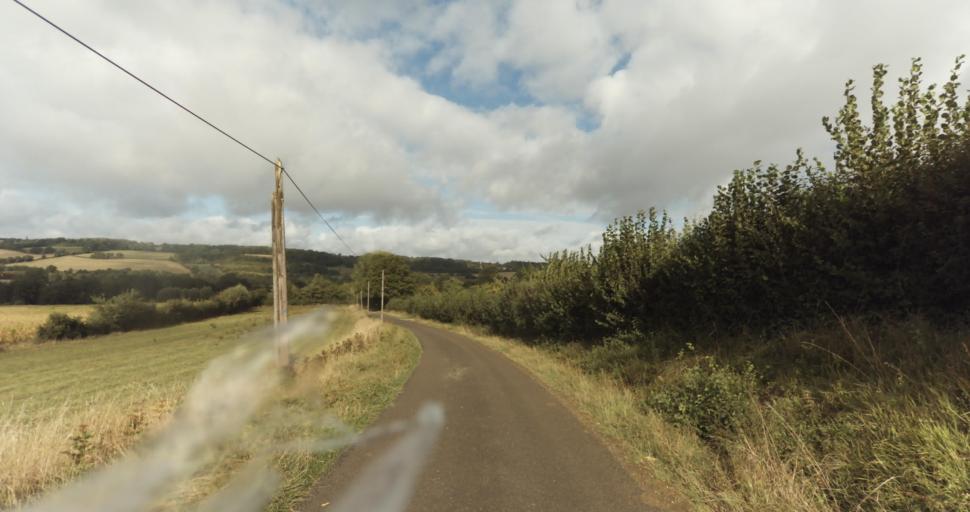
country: FR
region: Lower Normandy
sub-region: Departement de l'Orne
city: Gace
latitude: 48.8653
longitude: 0.2889
